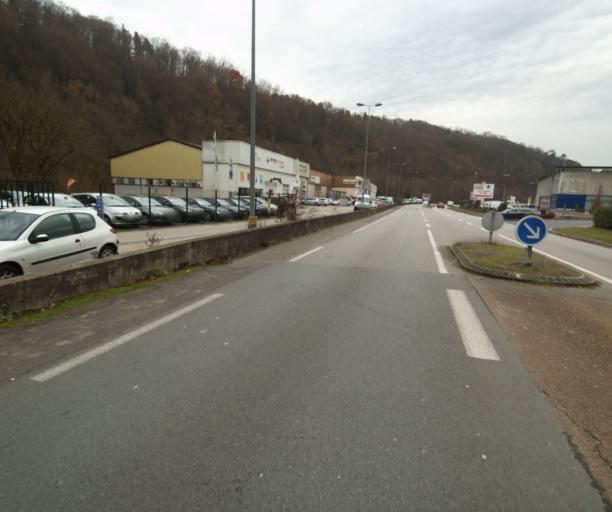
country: FR
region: Limousin
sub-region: Departement de la Correze
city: Tulle
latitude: 45.2433
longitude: 1.7443
